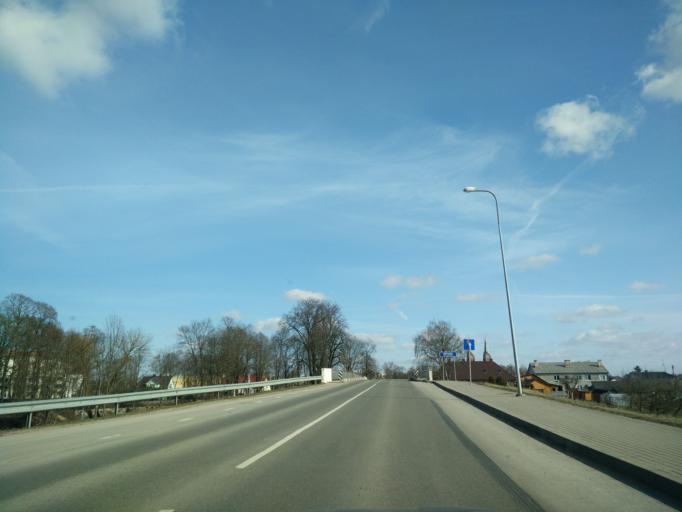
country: LT
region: Taurages apskritis
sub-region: Jurbarkas
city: Jurbarkas
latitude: 55.0773
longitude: 22.7545
